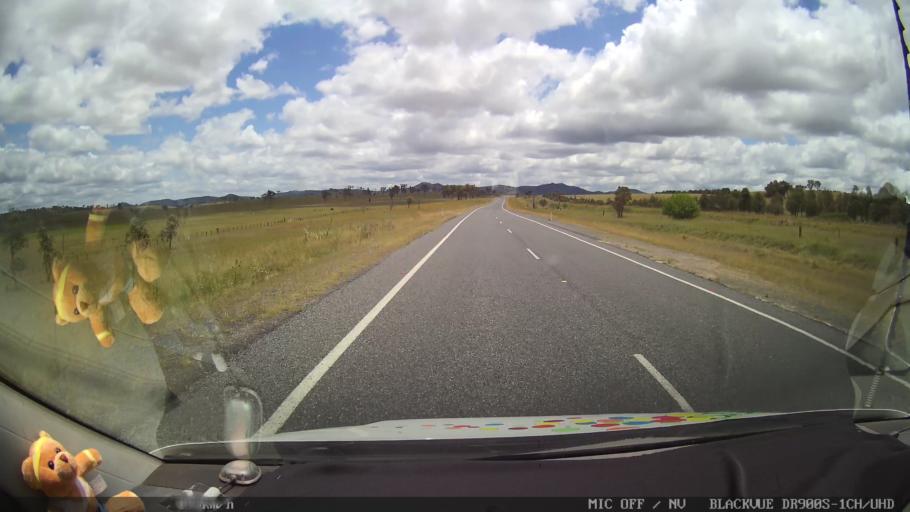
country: AU
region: New South Wales
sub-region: Glen Innes Severn
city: Glen Innes
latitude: -29.4006
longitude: 151.8743
